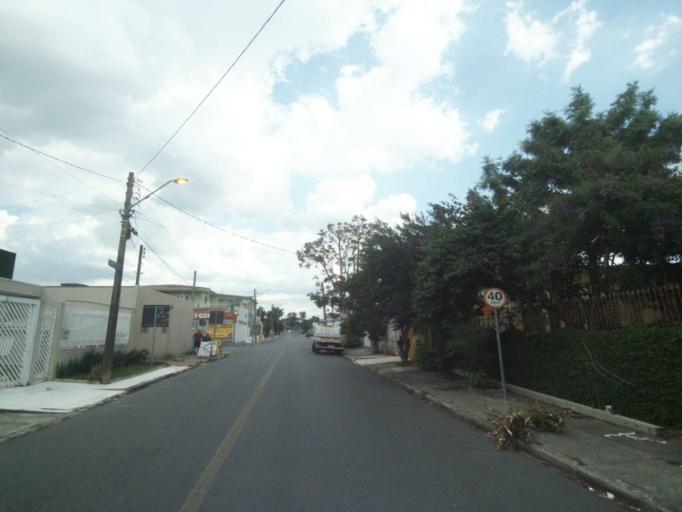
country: BR
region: Parana
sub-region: Sao Jose Dos Pinhais
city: Sao Jose dos Pinhais
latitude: -25.5299
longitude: -49.2709
